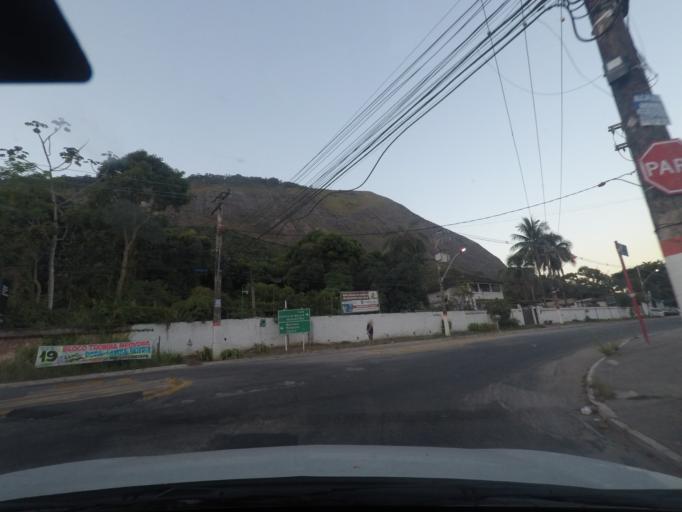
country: BR
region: Rio de Janeiro
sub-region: Marica
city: Marica
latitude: -22.9449
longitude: -42.9623
